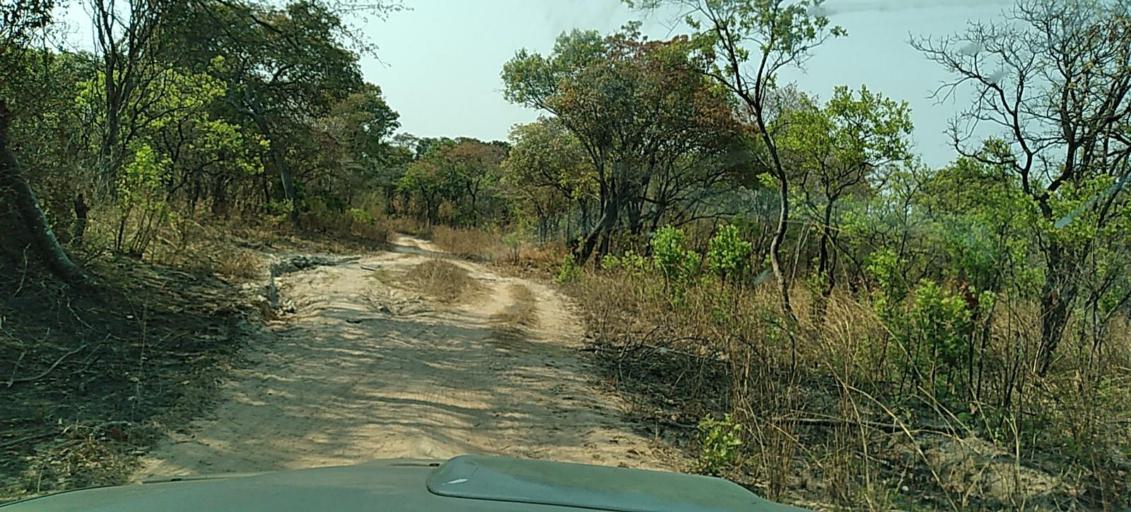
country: ZM
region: North-Western
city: Kasempa
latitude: -13.5364
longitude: 26.4086
